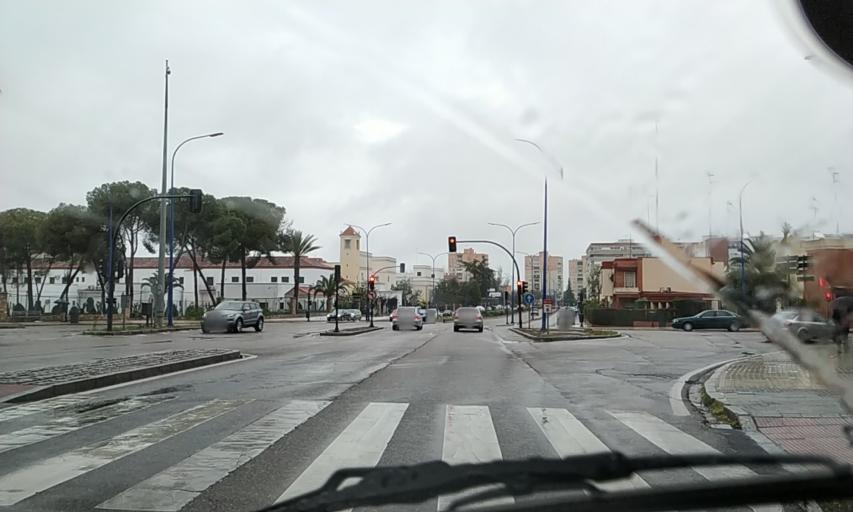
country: ES
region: Extremadura
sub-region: Provincia de Badajoz
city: Badajoz
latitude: 38.8704
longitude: -6.9781
